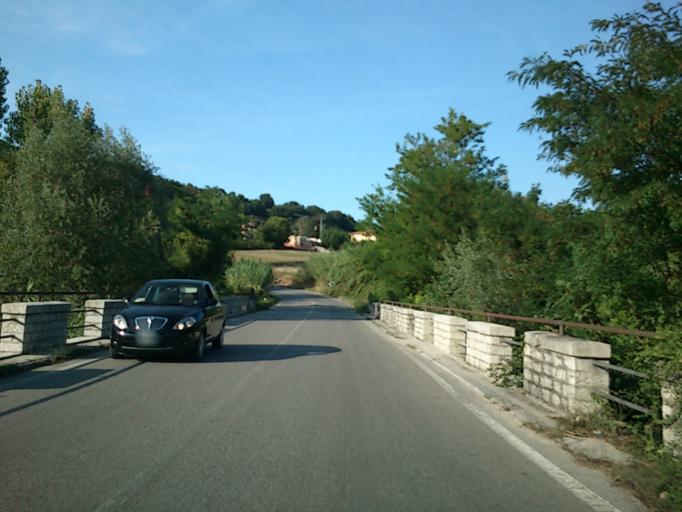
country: IT
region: The Marches
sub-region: Provincia di Pesaro e Urbino
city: Tavernelle
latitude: 43.7271
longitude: 12.8780
